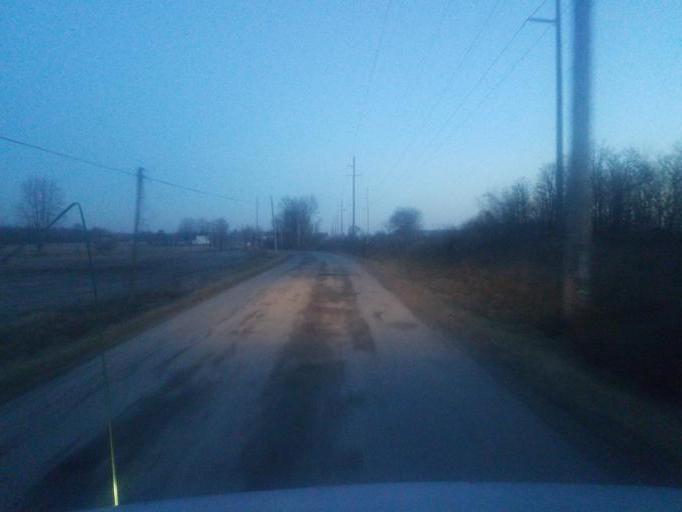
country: US
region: Ohio
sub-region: Morrow County
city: Mount Gilead
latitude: 40.6161
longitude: -82.8422
